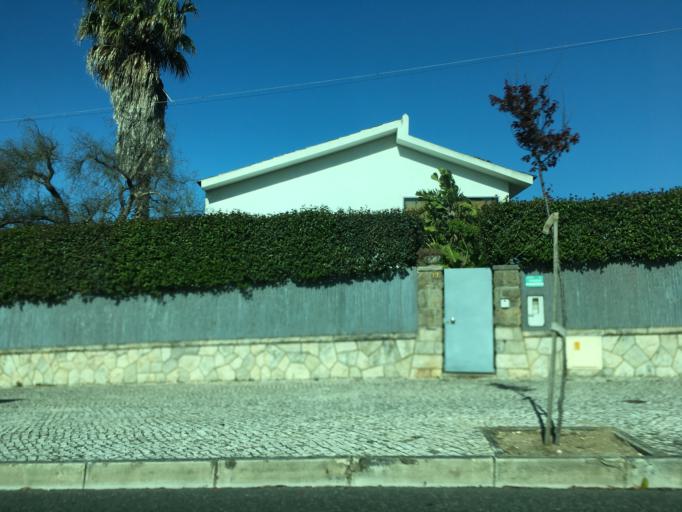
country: PT
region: Lisbon
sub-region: Cascais
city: Monte Estoril
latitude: 38.7118
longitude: -9.4178
